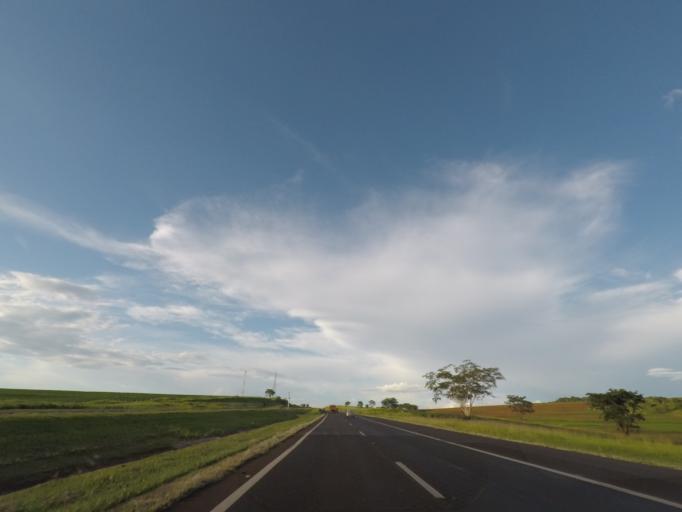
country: BR
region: Sao Paulo
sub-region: Ituverava
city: Ituverava
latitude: -20.2777
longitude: -47.7974
